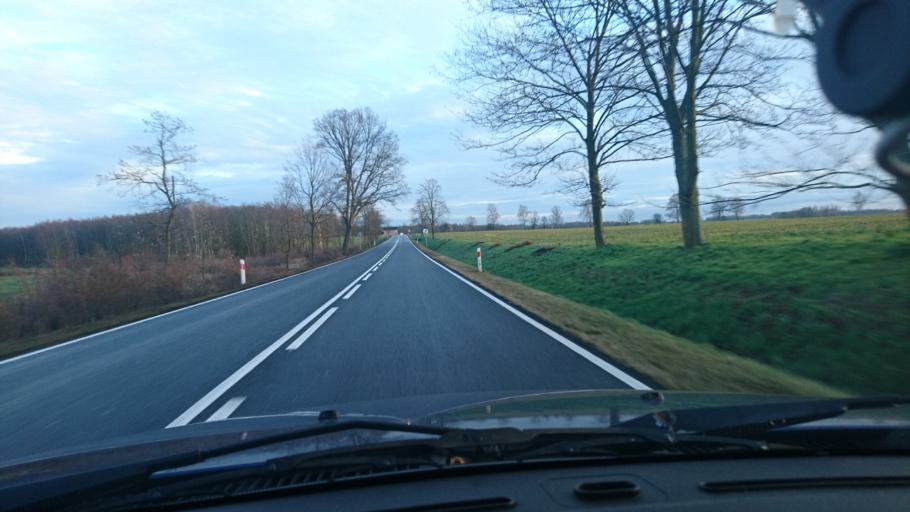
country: PL
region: Lodz Voivodeship
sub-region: Powiat wieruszowski
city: Boleslawiec
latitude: 51.1554
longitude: 18.1748
